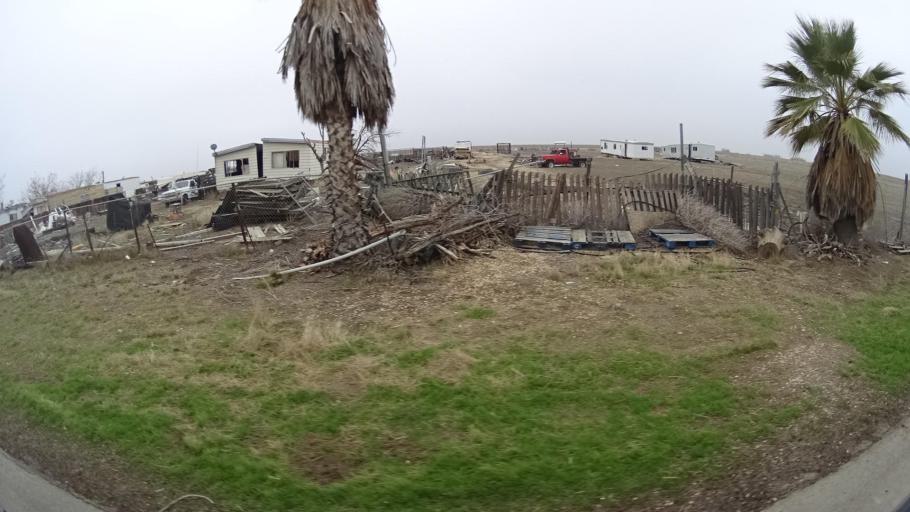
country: US
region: California
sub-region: Kern County
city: Wasco
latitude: 35.6840
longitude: -119.5086
